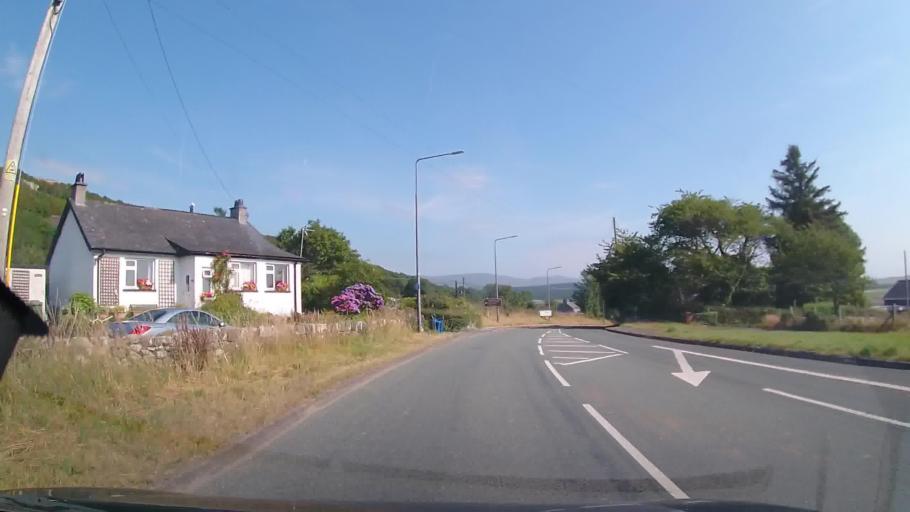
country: GB
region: Wales
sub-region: Gwynedd
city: Llanfair
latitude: 52.8390
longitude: -4.1134
